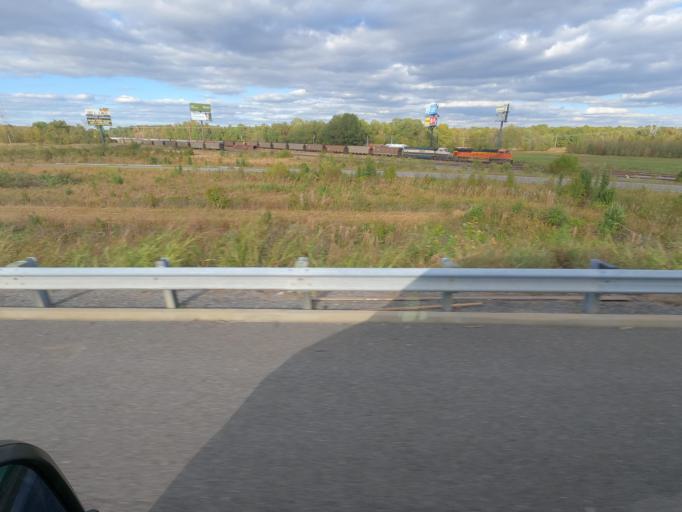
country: US
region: Kentucky
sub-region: McCracken County
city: Hendron
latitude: 37.0271
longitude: -88.6112
